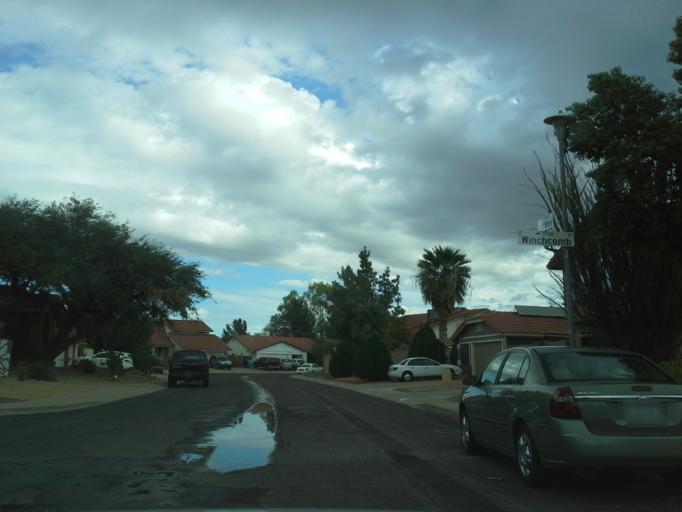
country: US
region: Arizona
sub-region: Maricopa County
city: Paradise Valley
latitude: 33.6167
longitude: -112.0380
